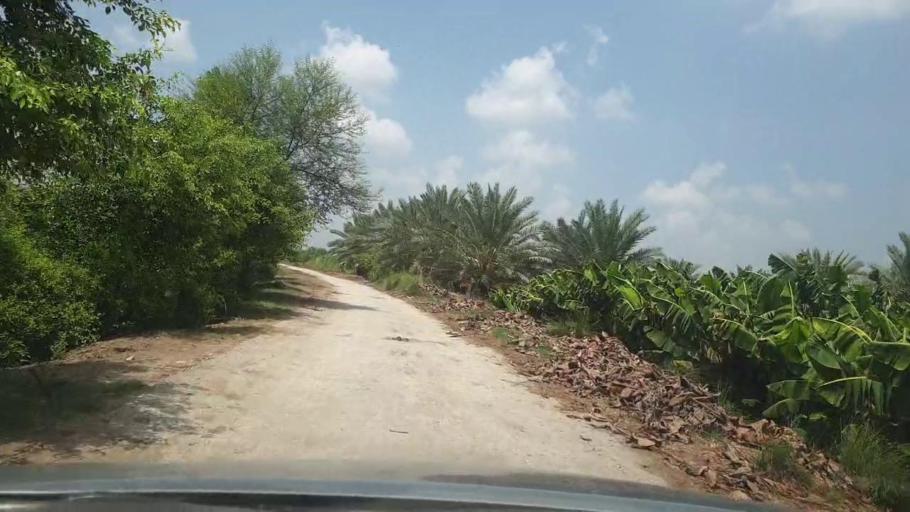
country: PK
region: Sindh
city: Pir jo Goth
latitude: 27.6027
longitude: 68.6128
